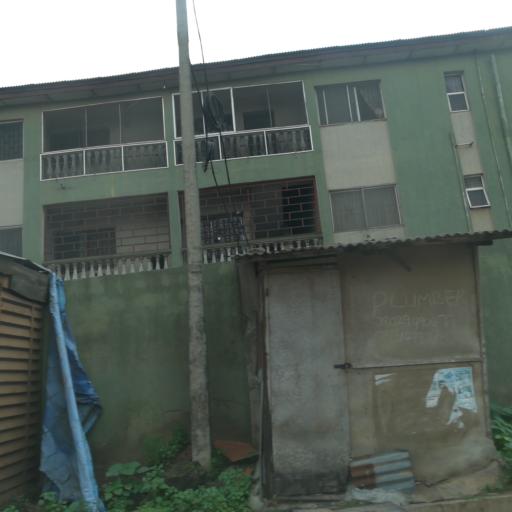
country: NG
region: Lagos
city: Agege
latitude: 6.5977
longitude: 3.2951
